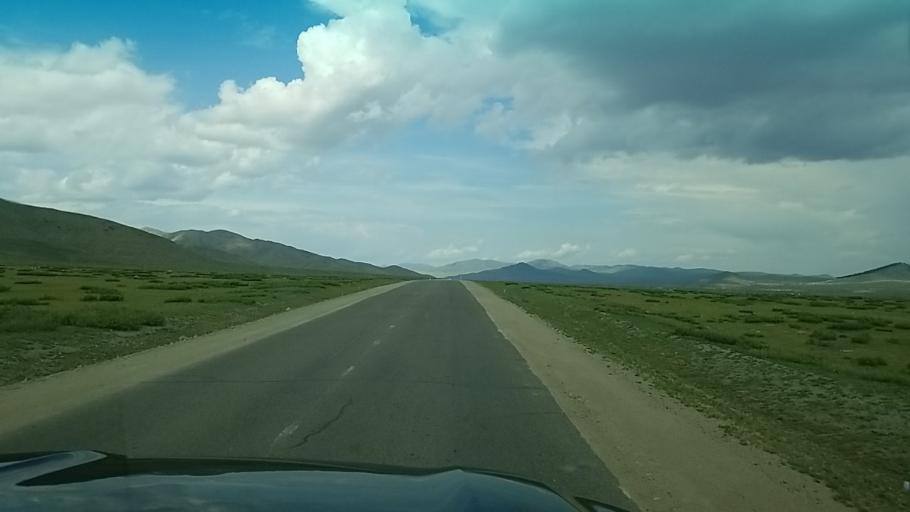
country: MN
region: Darhan Uul
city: Orhon
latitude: 49.7072
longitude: 106.0913
